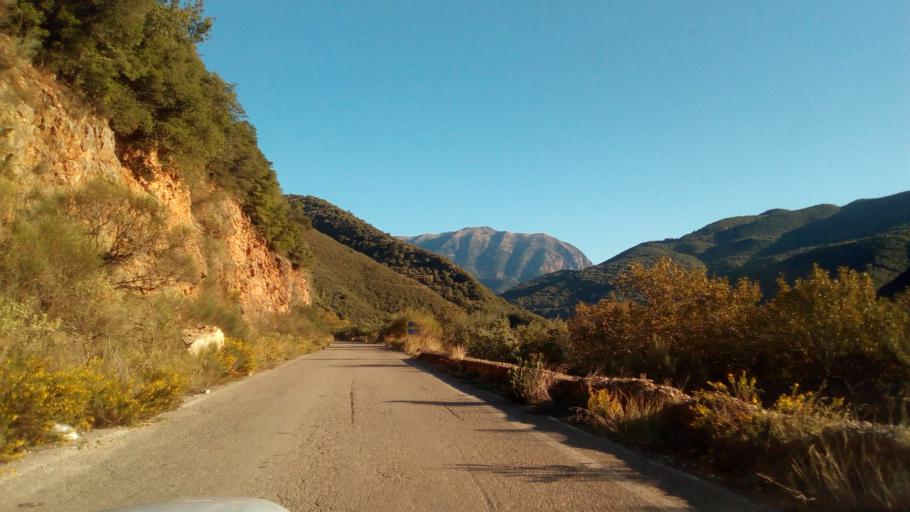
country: GR
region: West Greece
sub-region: Nomos Aitolias kai Akarnanias
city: Nafpaktos
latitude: 38.4346
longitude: 21.8784
